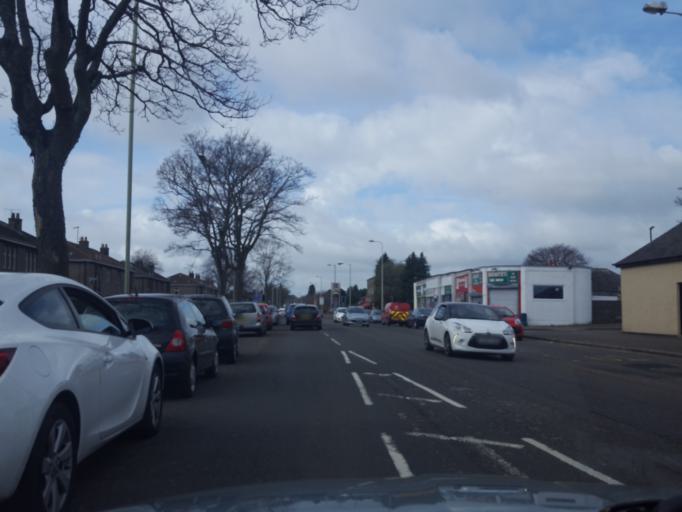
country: GB
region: Scotland
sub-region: Fife
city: Newport-On-Tay
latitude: 56.4735
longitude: -2.9264
